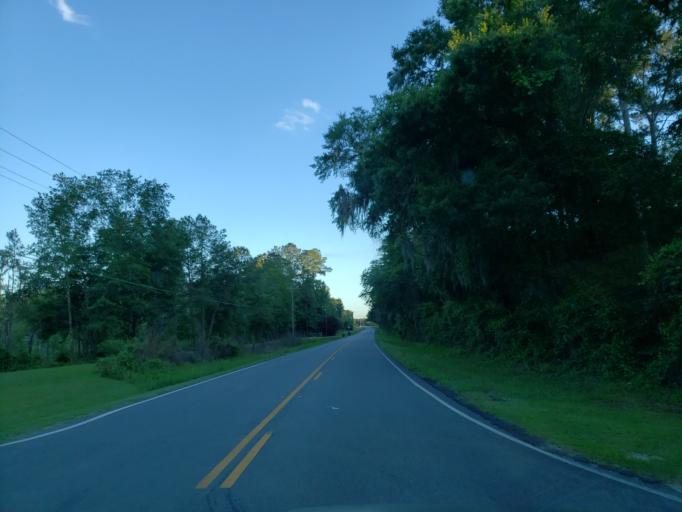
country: US
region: Georgia
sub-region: Lowndes County
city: Valdosta
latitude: 30.7315
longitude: -83.2489
